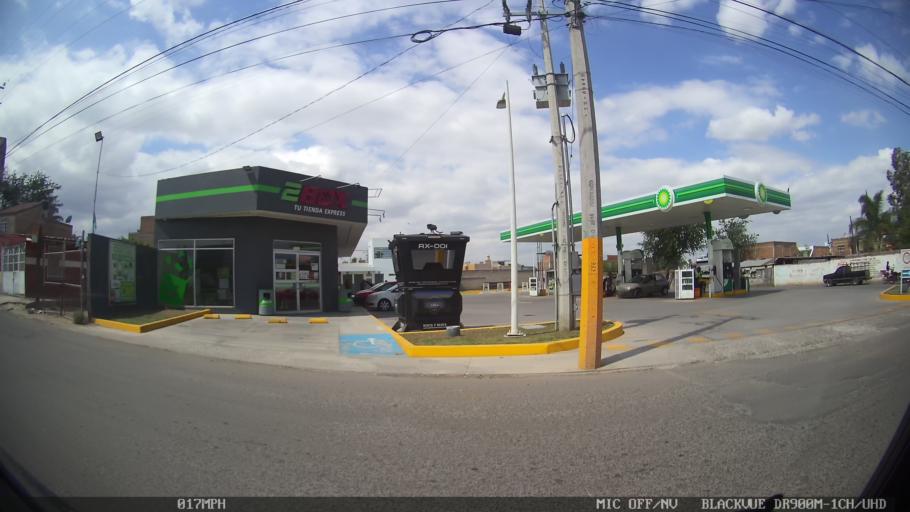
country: MX
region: Jalisco
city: Tonala
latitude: 20.6412
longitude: -103.2586
